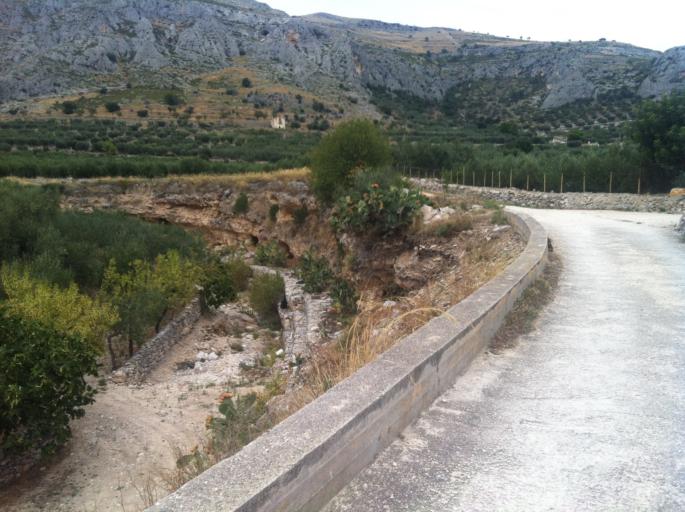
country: IT
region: Apulia
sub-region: Provincia di Foggia
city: Manfredonia
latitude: 41.6614
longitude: 15.9133
